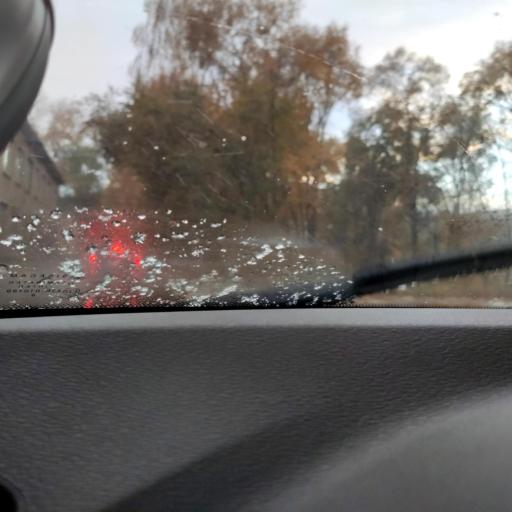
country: RU
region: Samara
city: Smyshlyayevka
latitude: 53.2184
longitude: 50.2741
